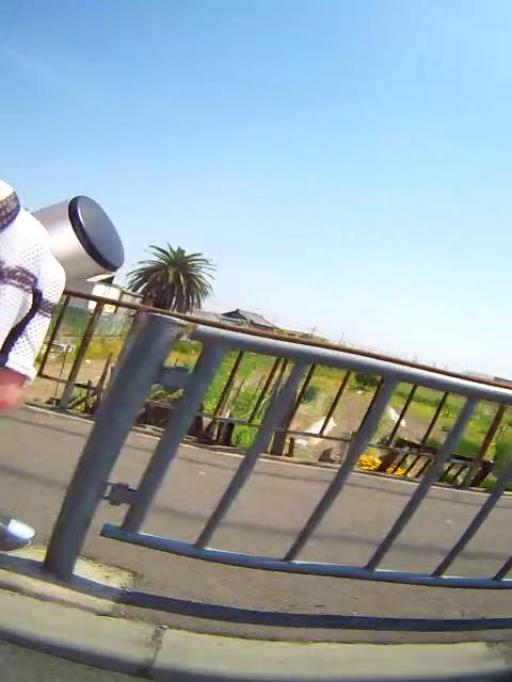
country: JP
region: Osaka
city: Matsubara
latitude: 34.5345
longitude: 135.5636
